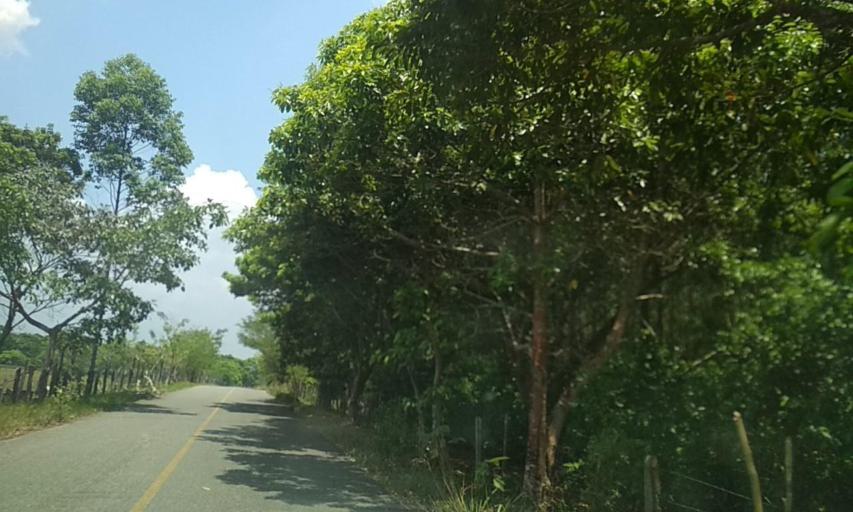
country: MX
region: Tabasco
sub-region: Huimanguillo
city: Francisco Rueda
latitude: 17.8373
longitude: -93.9116
